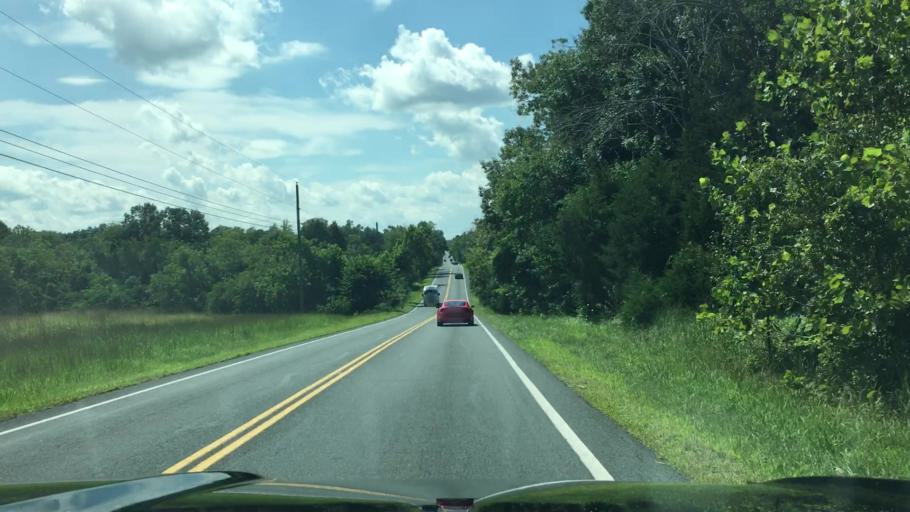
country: US
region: Virginia
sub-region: Prince William County
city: Bull Run
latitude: 38.8158
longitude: -77.5373
